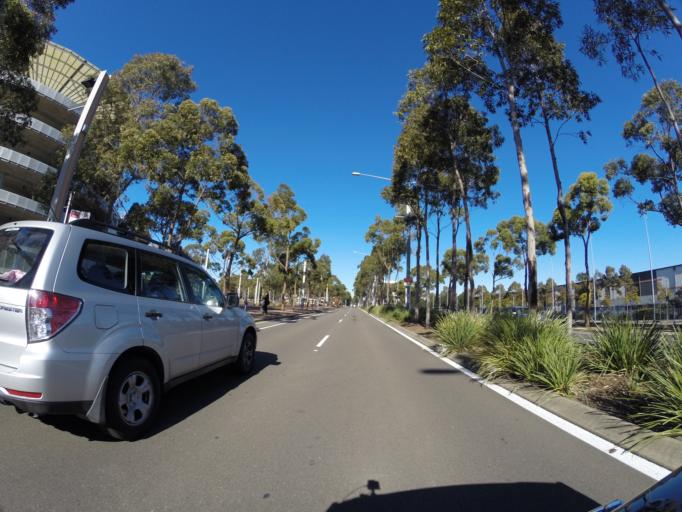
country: AU
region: New South Wales
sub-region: Canada Bay
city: Concord West
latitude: -33.8476
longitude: 151.0612
